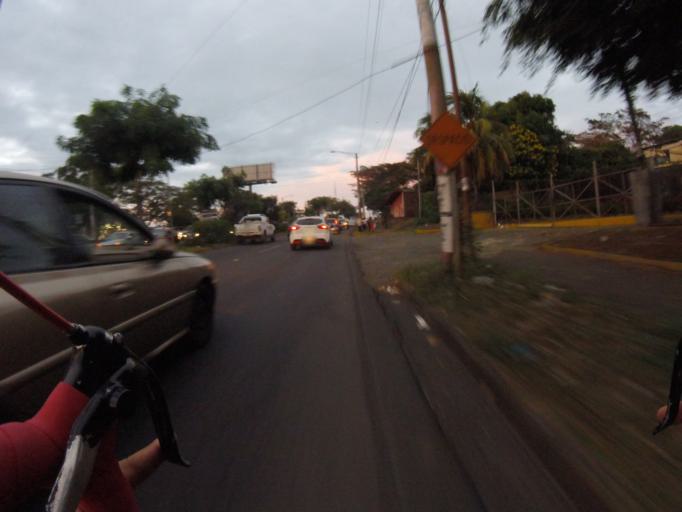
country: NI
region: Managua
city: Managua
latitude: 12.1370
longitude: -86.2754
